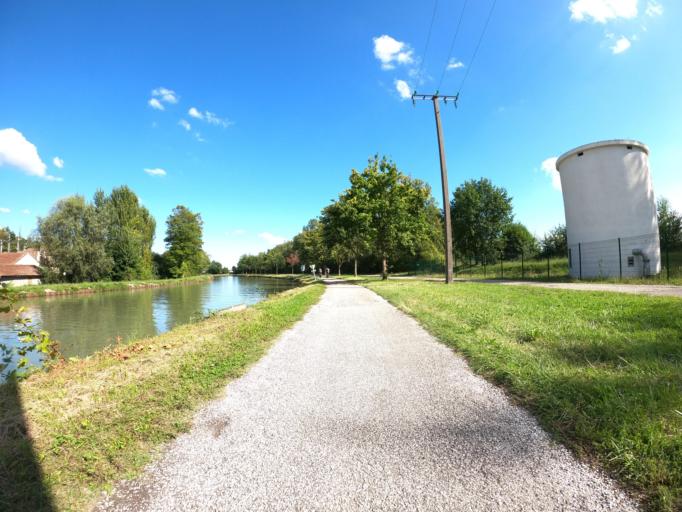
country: FR
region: Midi-Pyrenees
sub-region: Departement du Tarn-et-Garonne
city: Saint-Nicolas-de-la-Grave
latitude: 44.0835
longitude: 0.9808
